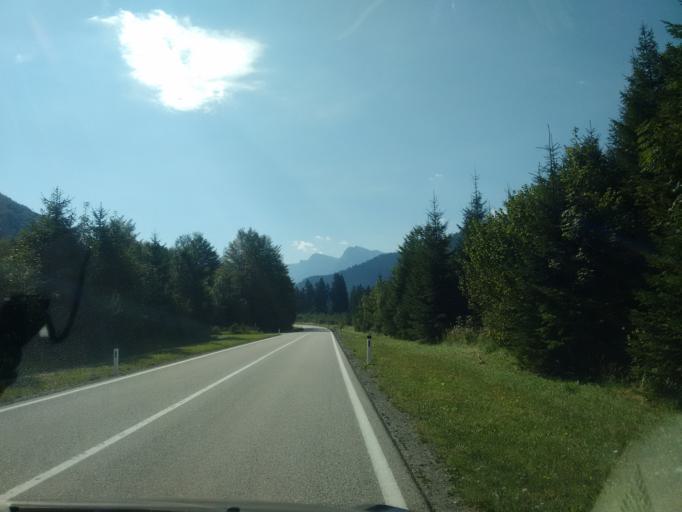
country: AT
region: Upper Austria
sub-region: Politischer Bezirk Gmunden
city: Gruenau im Almtal
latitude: 47.8060
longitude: 13.9515
